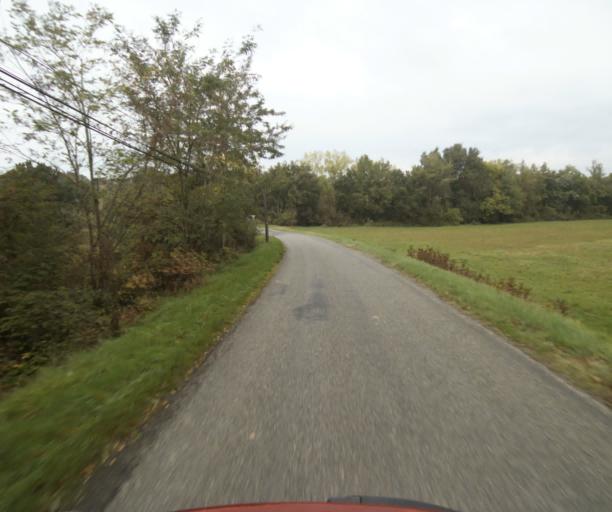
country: FR
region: Midi-Pyrenees
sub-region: Departement du Tarn-et-Garonne
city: Verdun-sur-Garonne
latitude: 43.8377
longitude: 1.1949
